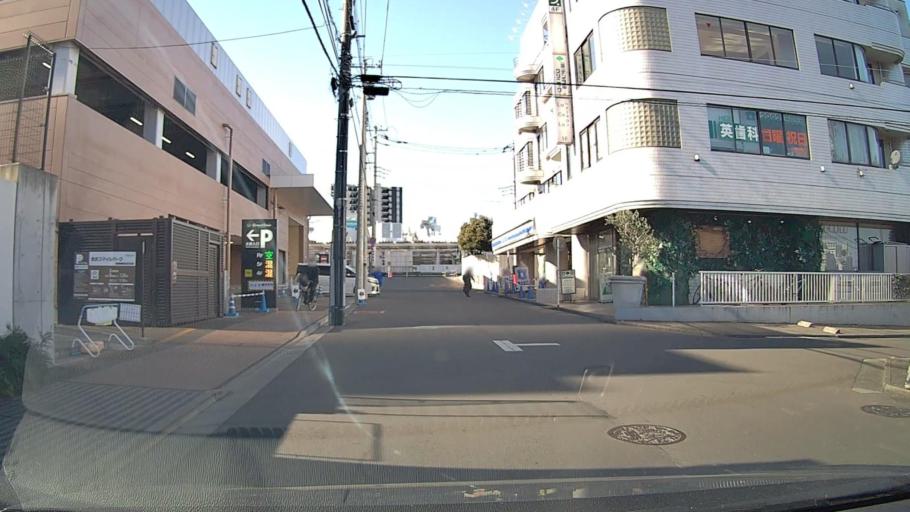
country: JP
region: Saitama
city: Tokorozawa
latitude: 35.7878
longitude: 139.4750
